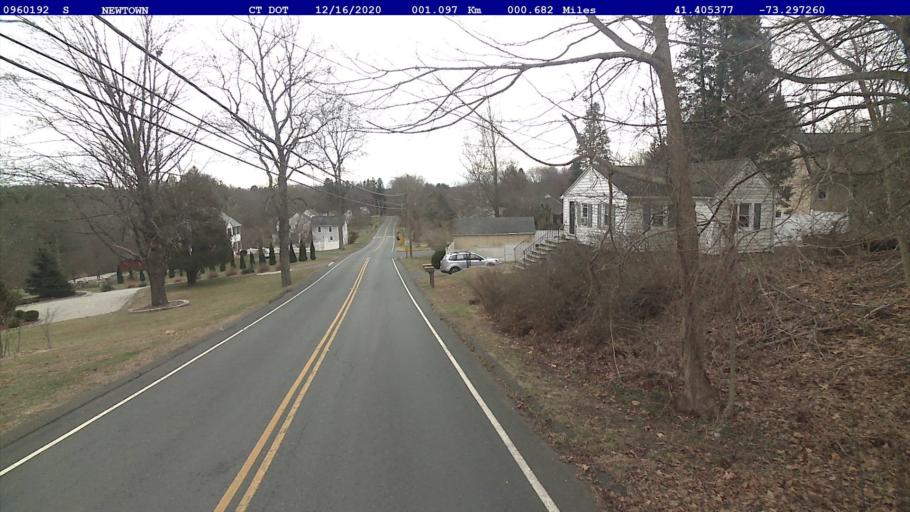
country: US
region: Connecticut
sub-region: Fairfield County
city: Newtown
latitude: 41.4054
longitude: -73.2973
